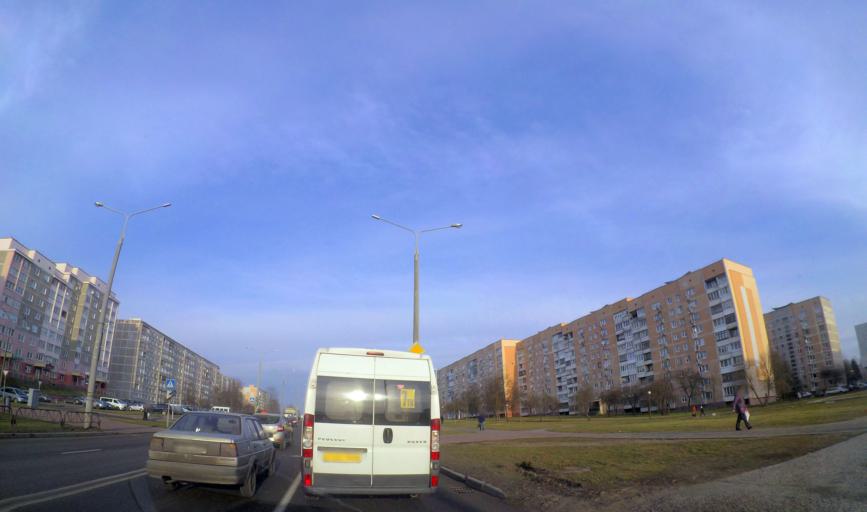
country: BY
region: Grodnenskaya
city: Hrodna
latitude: 53.6611
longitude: 23.7827
